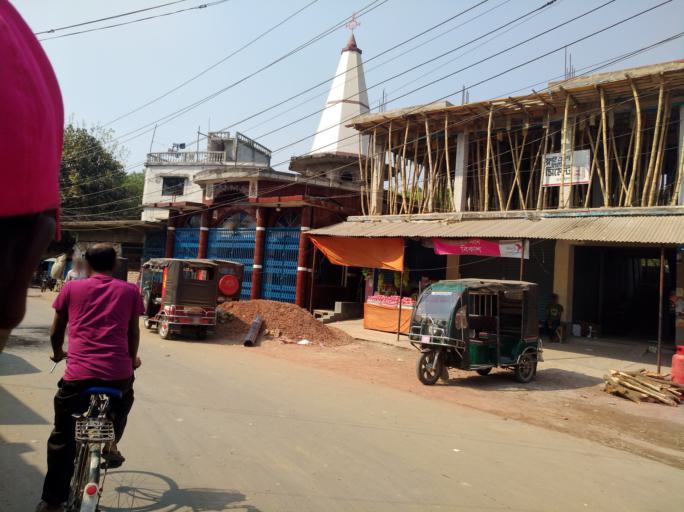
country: BD
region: Khulna
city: Kaliganj
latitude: 23.5497
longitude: 89.1675
